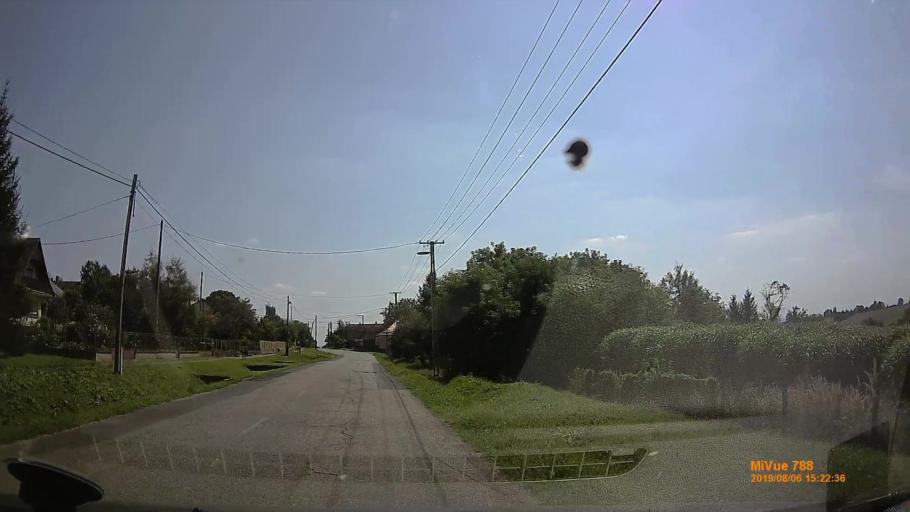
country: HR
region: Koprivnicko-Krizevacka
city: Drnje
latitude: 46.2675
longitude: 16.9460
